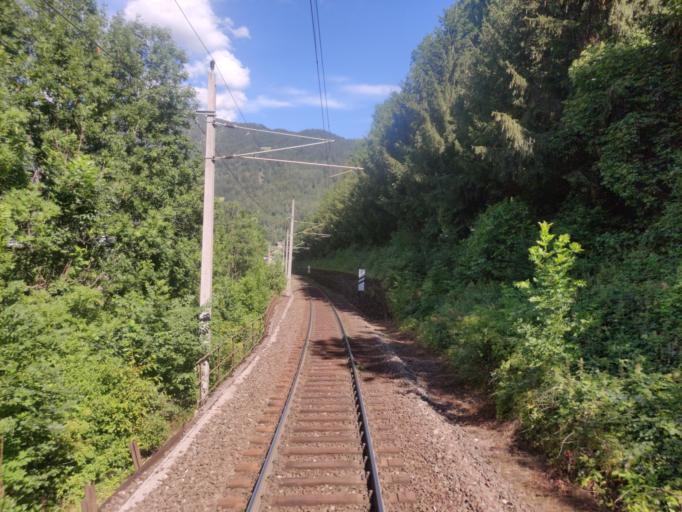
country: AT
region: Tyrol
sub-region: Politischer Bezirk Landeck
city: Stanz bei Landeck
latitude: 47.1388
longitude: 10.5562
